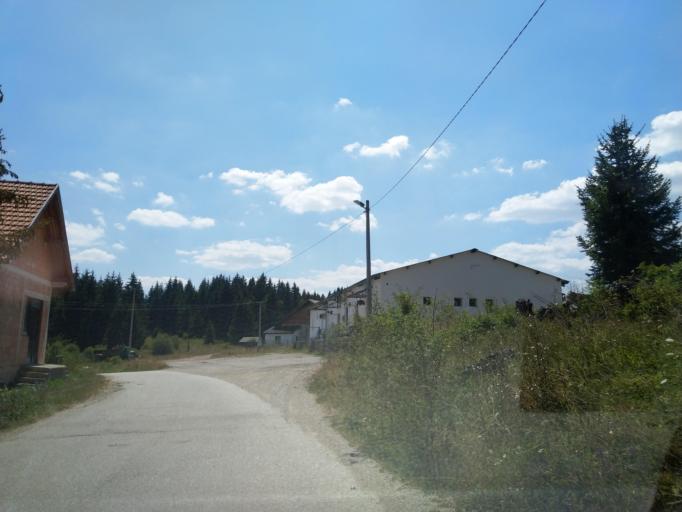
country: RS
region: Central Serbia
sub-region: Zlatiborski Okrug
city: Nova Varos
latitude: 43.4669
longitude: 19.9719
